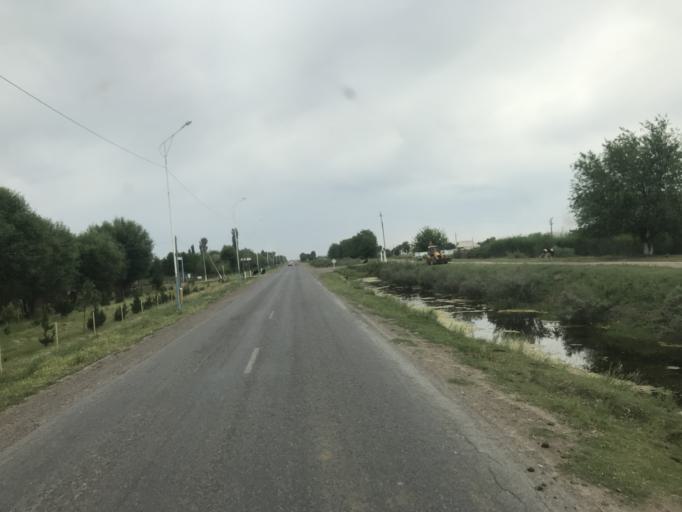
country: KZ
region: Ongtustik Qazaqstan
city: Asykata
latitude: 40.9307
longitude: 68.4070
